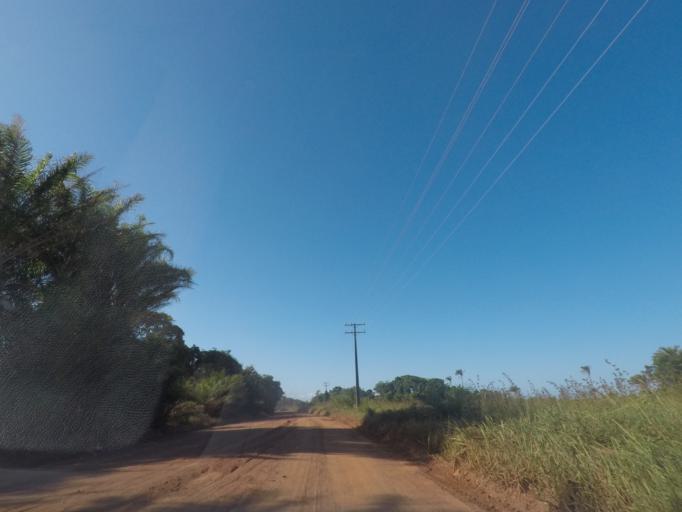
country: BR
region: Bahia
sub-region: Camamu
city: Camamu
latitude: -13.9483
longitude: -38.9454
